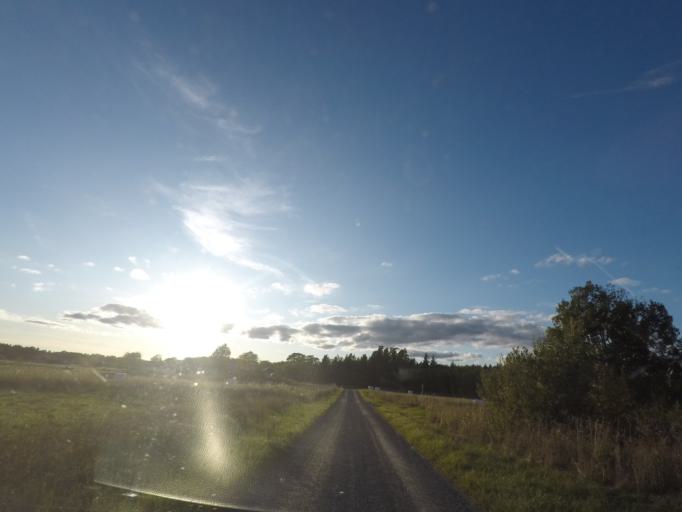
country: SE
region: Vaestmanland
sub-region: Hallstahammars Kommun
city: Kolback
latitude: 59.4795
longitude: 16.2031
